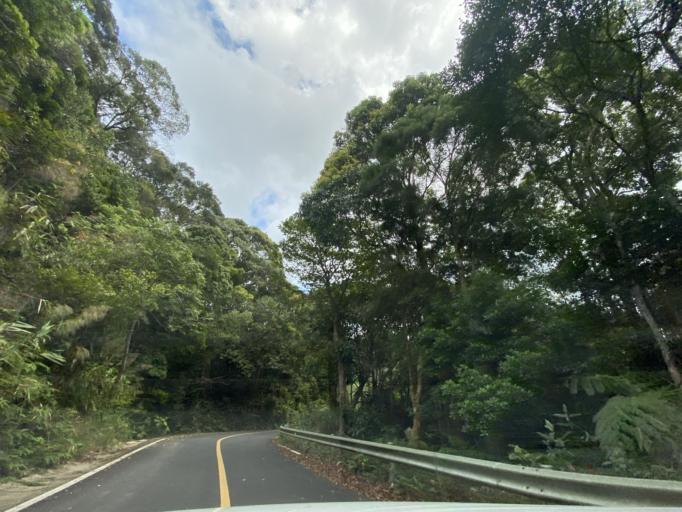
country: CN
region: Hainan
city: Benhao
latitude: 18.6982
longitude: 109.8816
